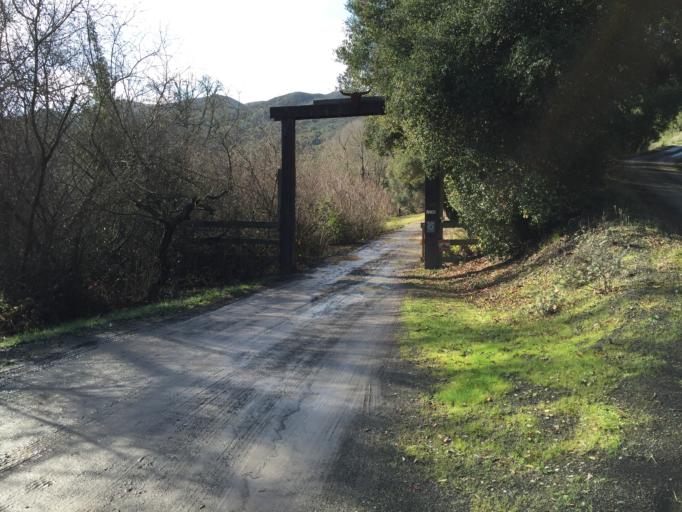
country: US
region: California
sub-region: San Luis Obispo County
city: Atascadero
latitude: 35.4618
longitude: -120.7725
